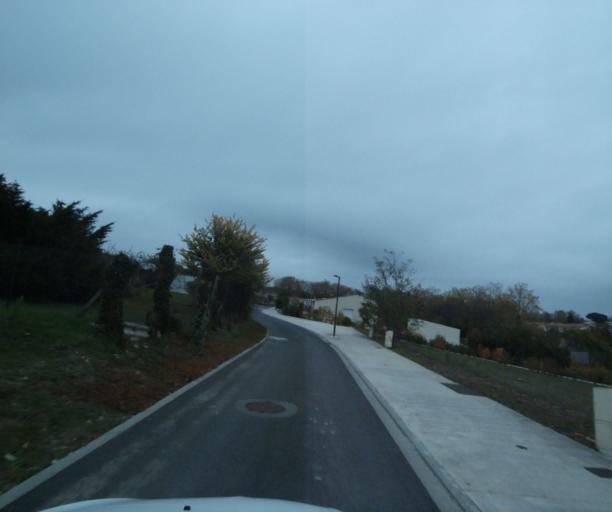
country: FR
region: Poitou-Charentes
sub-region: Departement de la Charente-Maritime
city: Saintes
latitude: 45.7449
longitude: -0.6084
